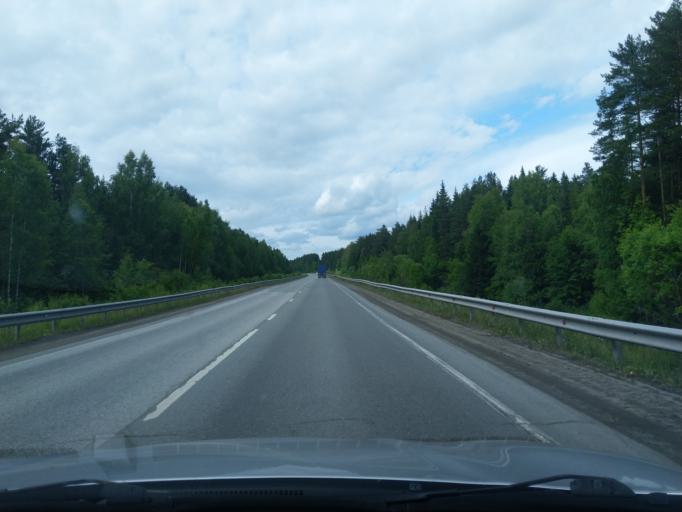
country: RU
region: Sverdlovsk
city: Nizhniy Tagil
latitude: 57.9531
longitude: 59.8726
